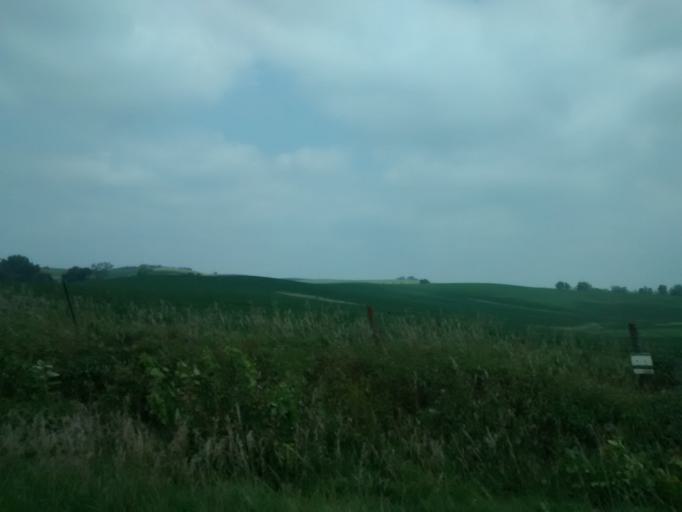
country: US
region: Iowa
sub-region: Woodbury County
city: Moville
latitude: 42.3352
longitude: -96.0452
